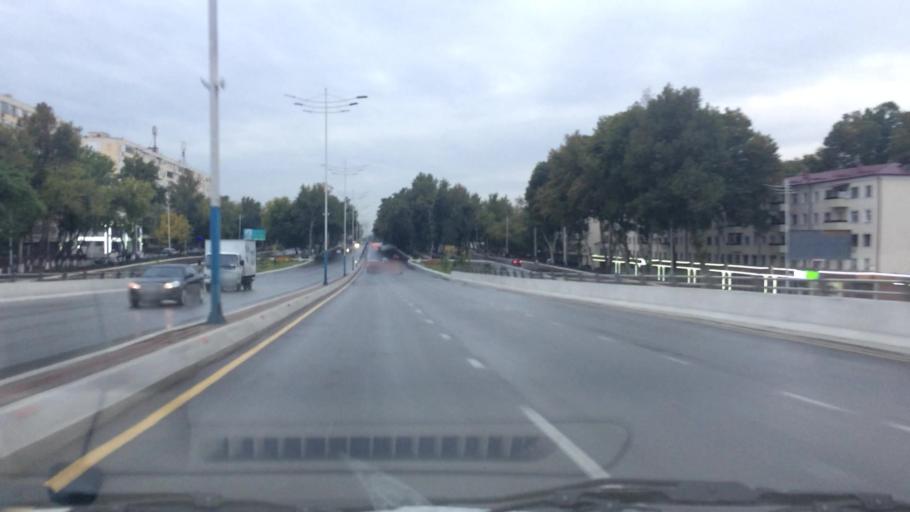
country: UZ
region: Toshkent Shahri
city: Tashkent
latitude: 41.2907
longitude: 69.2219
